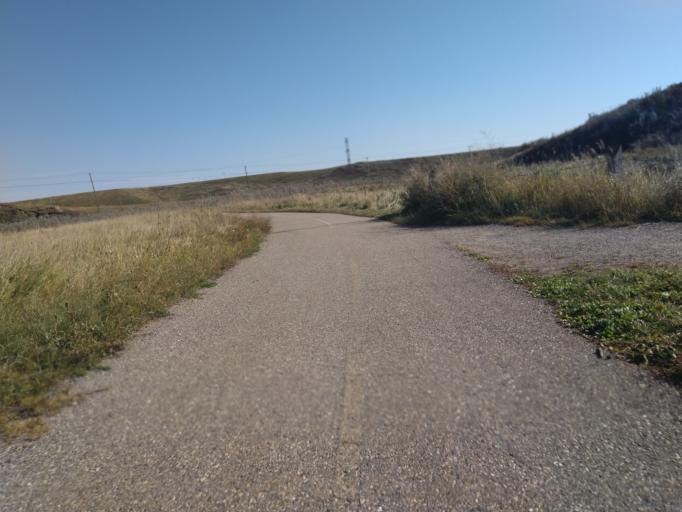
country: CA
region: Alberta
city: Calgary
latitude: 51.1331
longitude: -114.0511
